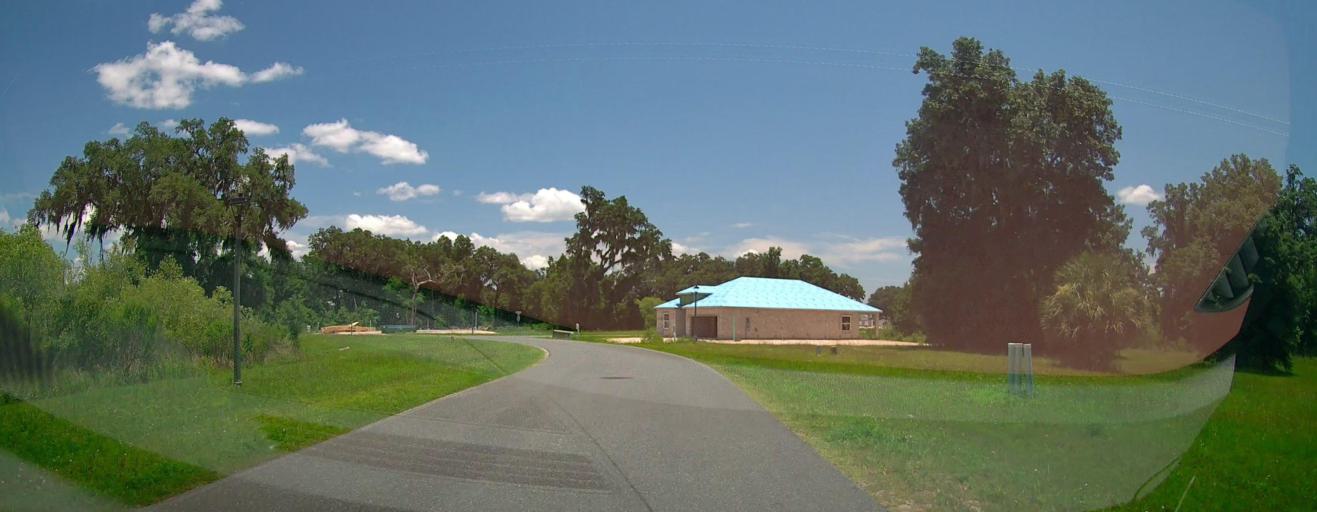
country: US
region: Florida
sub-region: Marion County
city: Belleview
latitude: 29.0910
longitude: -82.0711
